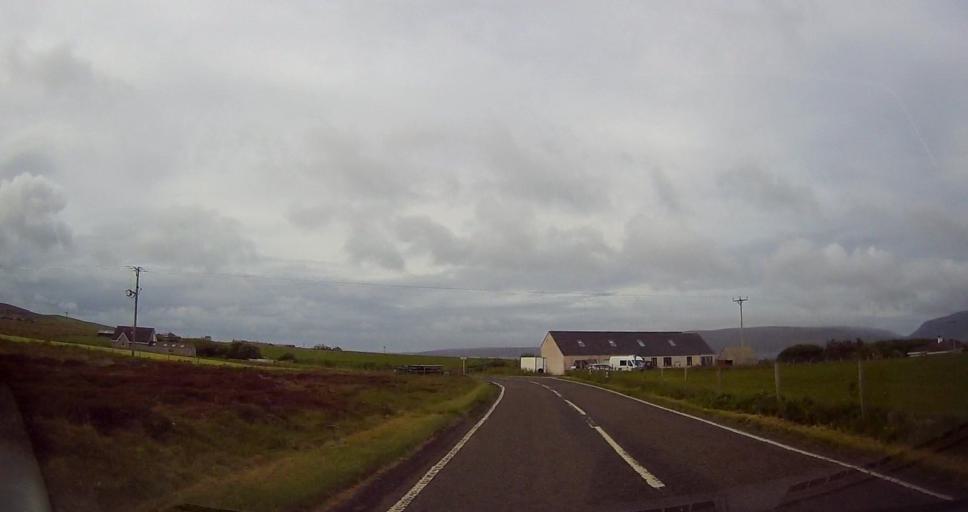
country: GB
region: Scotland
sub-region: Orkney Islands
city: Stromness
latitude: 58.9392
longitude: -3.2132
